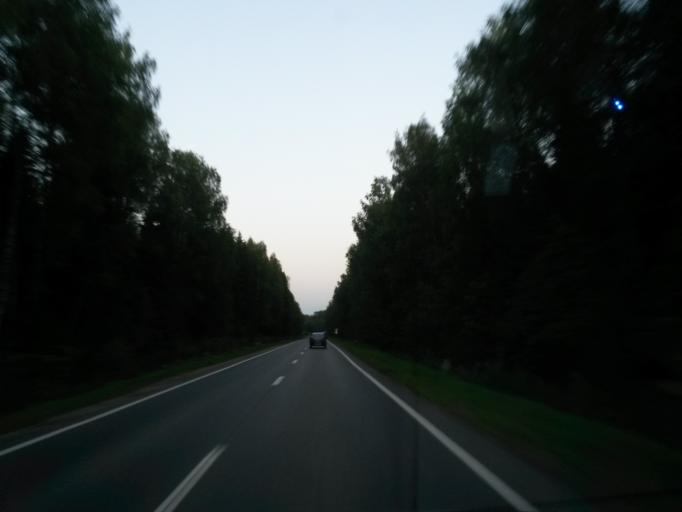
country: RU
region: Jaroslavl
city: Yaroslavl
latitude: 57.8016
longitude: 39.7921
